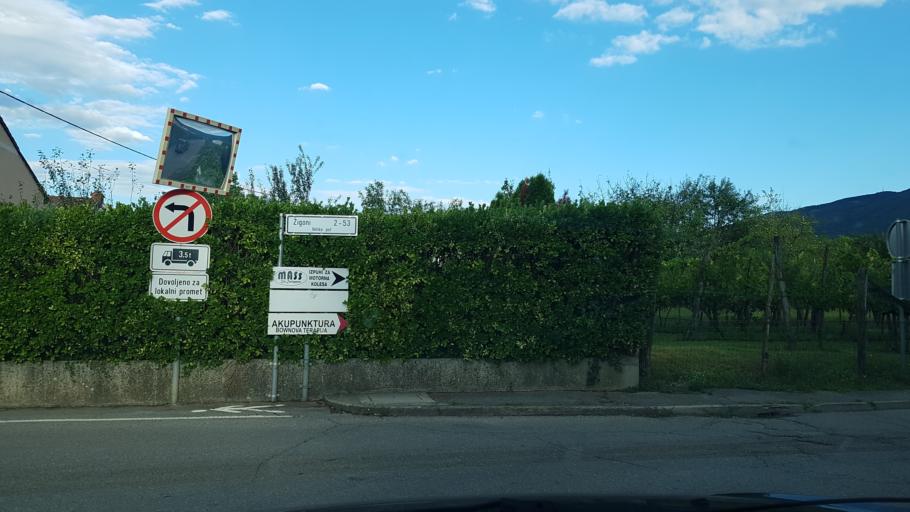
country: SI
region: Rence-Vogrsko
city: Rence
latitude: 45.8876
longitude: 13.6677
